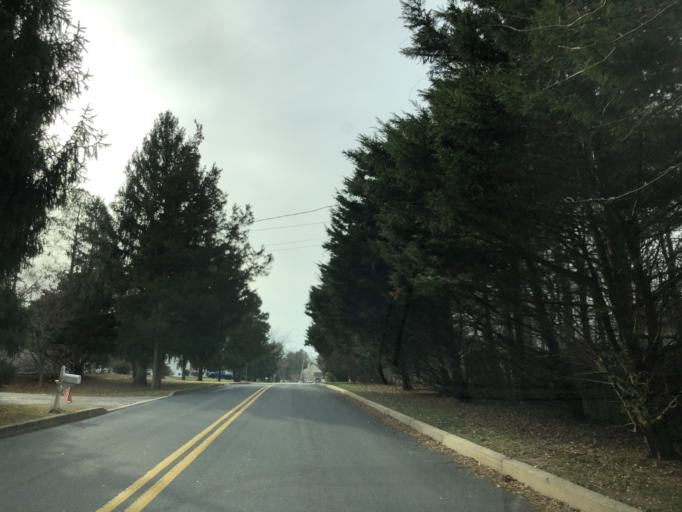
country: US
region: Pennsylvania
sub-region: Chester County
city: Exton
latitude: 40.0353
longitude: -75.6430
